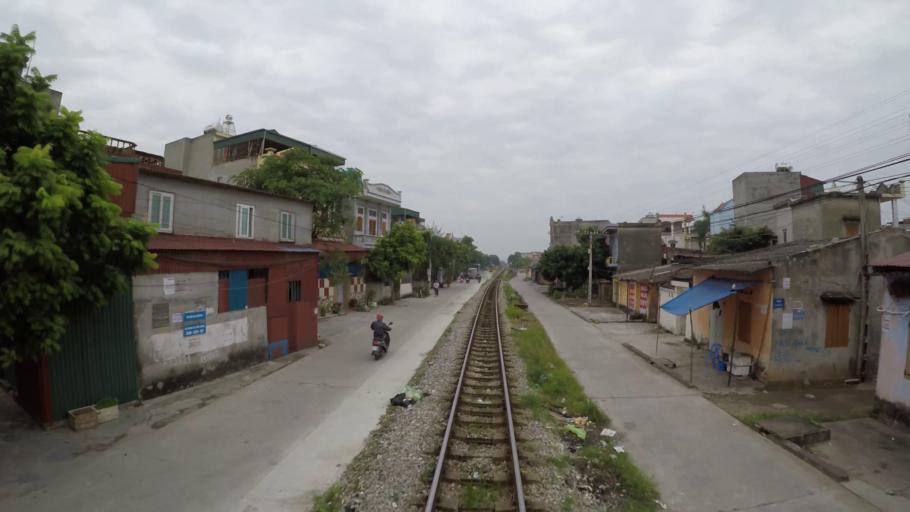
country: VN
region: Hai Duong
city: Thanh Pho Hai Duong
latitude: 20.9431
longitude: 106.2902
